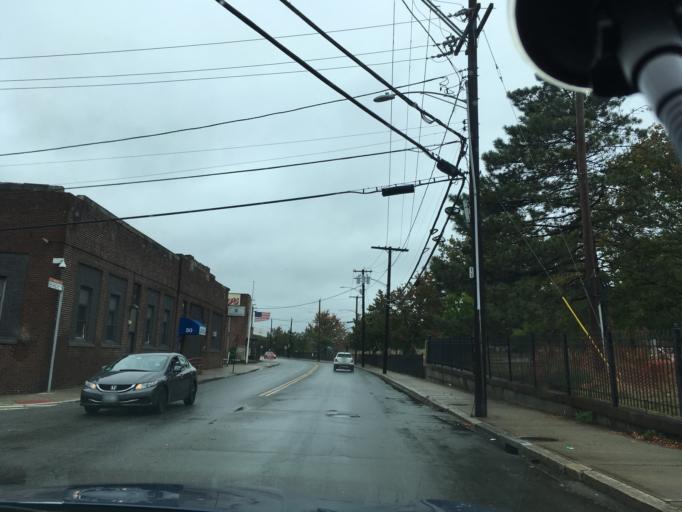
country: US
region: Rhode Island
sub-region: Providence County
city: Providence
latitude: 41.8428
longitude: -71.4084
